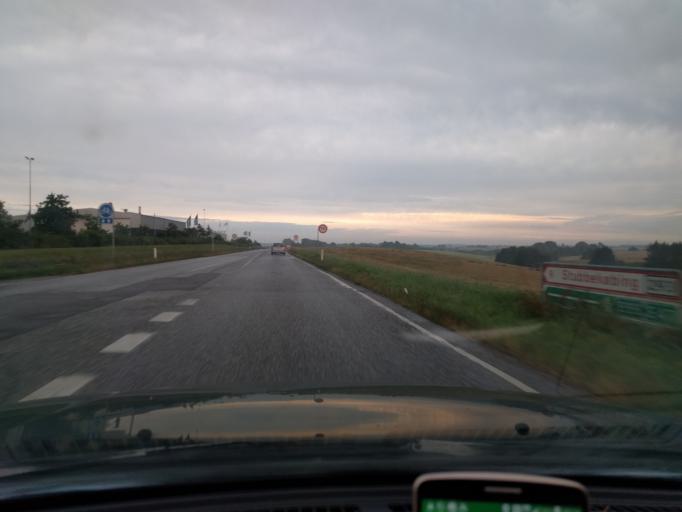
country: DK
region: Zealand
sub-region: Guldborgsund Kommune
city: Norre Alslev
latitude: 54.8991
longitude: 11.8936
